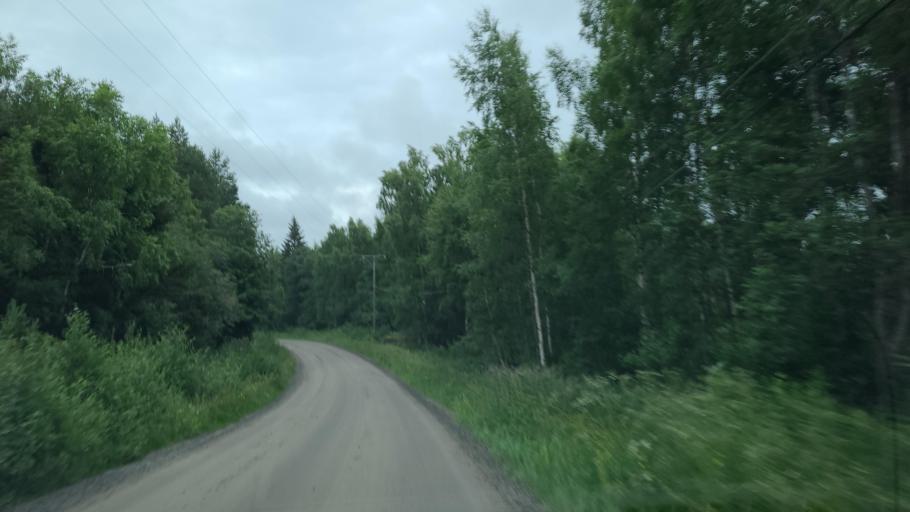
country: FI
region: Ostrobothnia
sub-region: Vaasa
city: Replot
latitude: 63.3002
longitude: 21.1450
